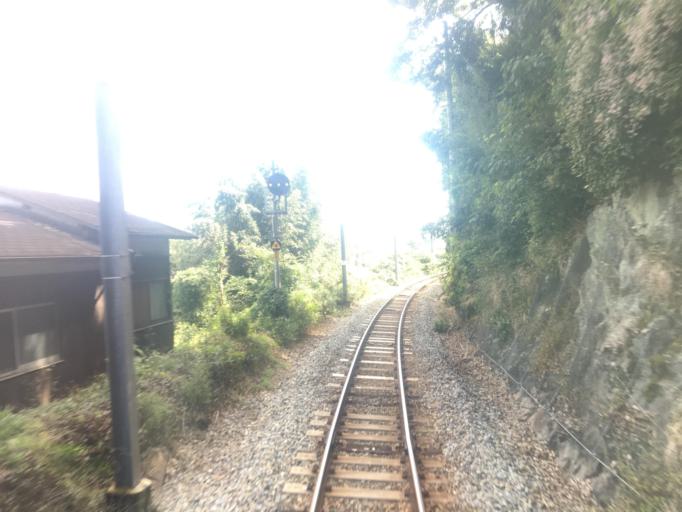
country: JP
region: Hyogo
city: Ono
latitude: 34.8230
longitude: 134.9328
